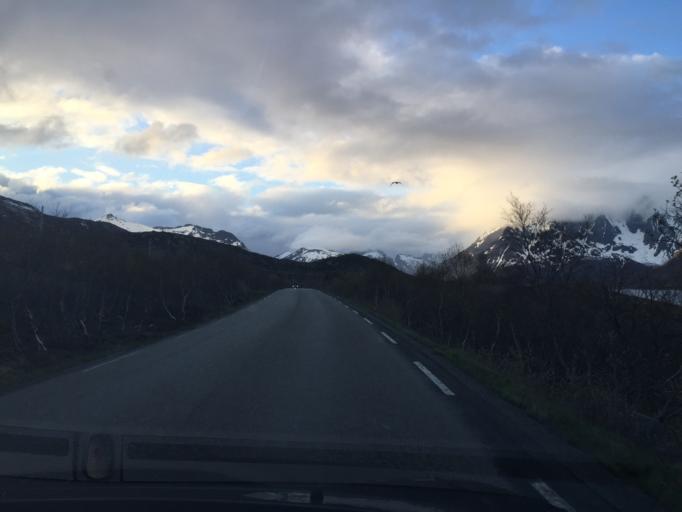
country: NO
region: Nordland
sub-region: Vagan
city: Svolvaer
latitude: 68.2901
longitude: 14.6967
